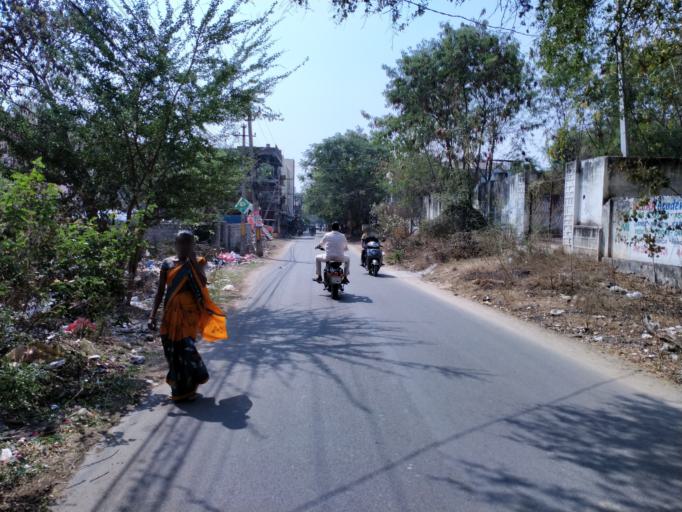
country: IN
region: Telangana
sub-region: Rangareddi
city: Secunderabad
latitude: 17.4992
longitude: 78.5466
